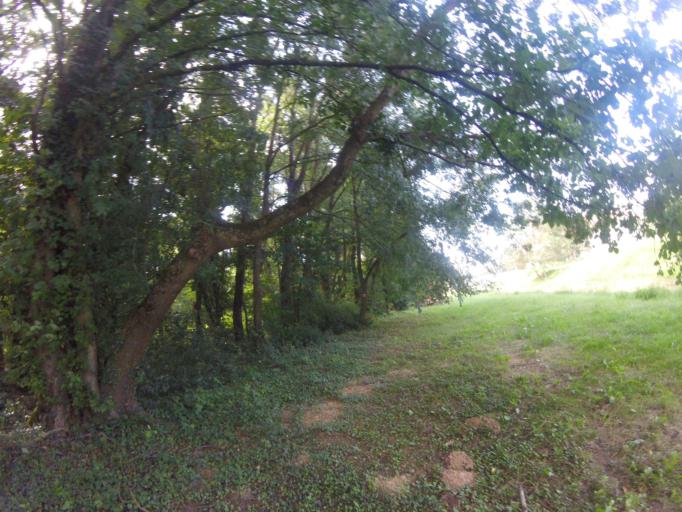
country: HU
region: Zala
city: Lenti
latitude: 46.6271
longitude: 16.5520
